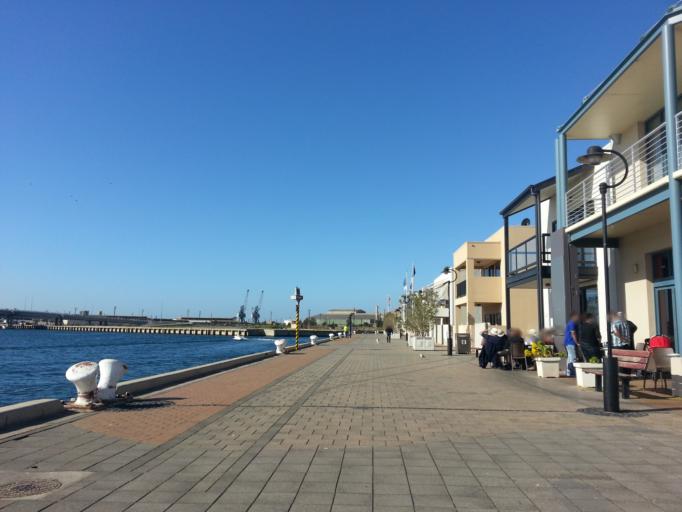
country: AU
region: South Australia
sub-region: Port Adelaide Enfield
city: Birkenhead
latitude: -34.8419
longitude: 138.5053
